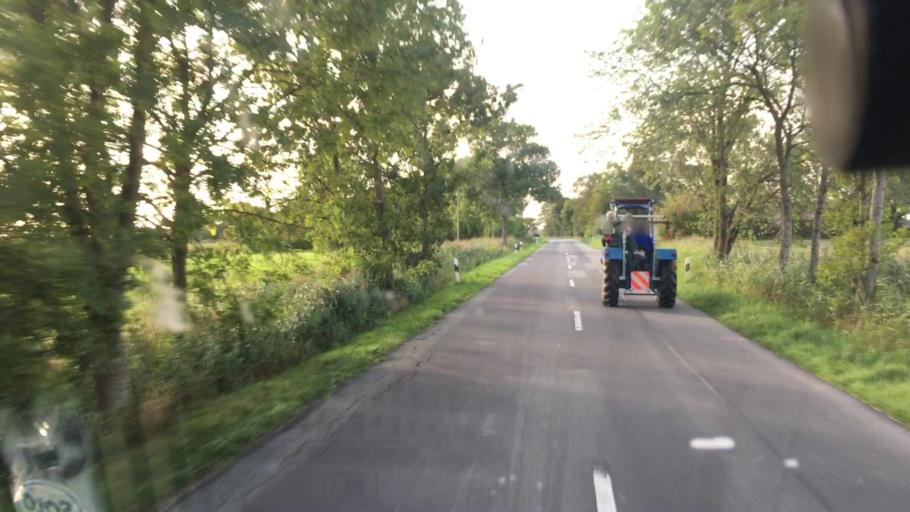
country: DE
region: Lower Saxony
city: Werdum
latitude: 53.6671
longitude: 7.7302
